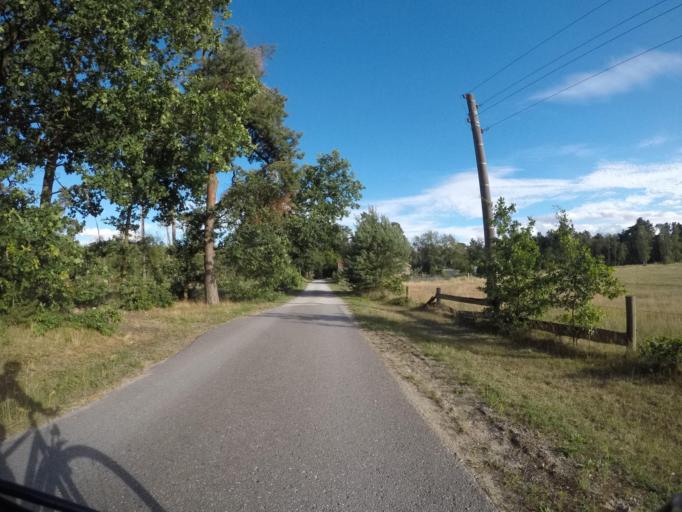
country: DE
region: Mecklenburg-Vorpommern
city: Lubtheen
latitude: 53.2329
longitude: 11.0446
